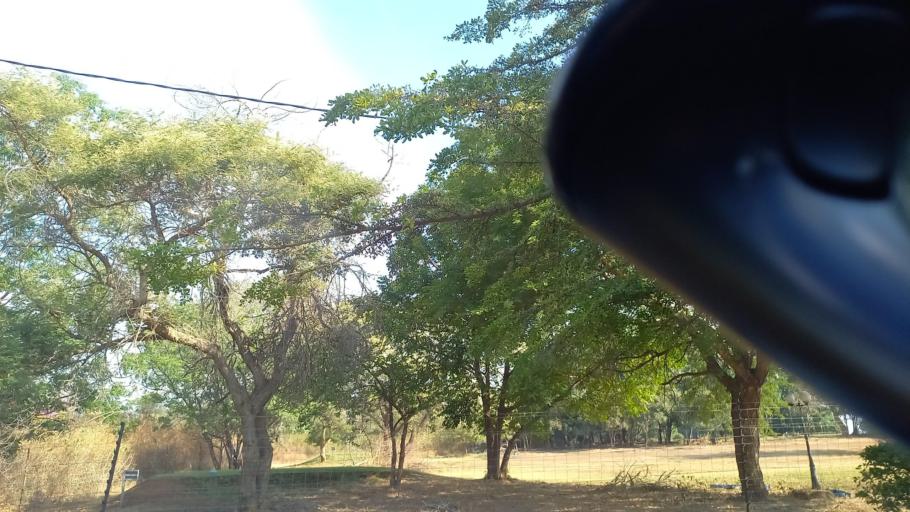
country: ZM
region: Southern
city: Mazabuka
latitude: -15.8635
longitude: 27.7605
